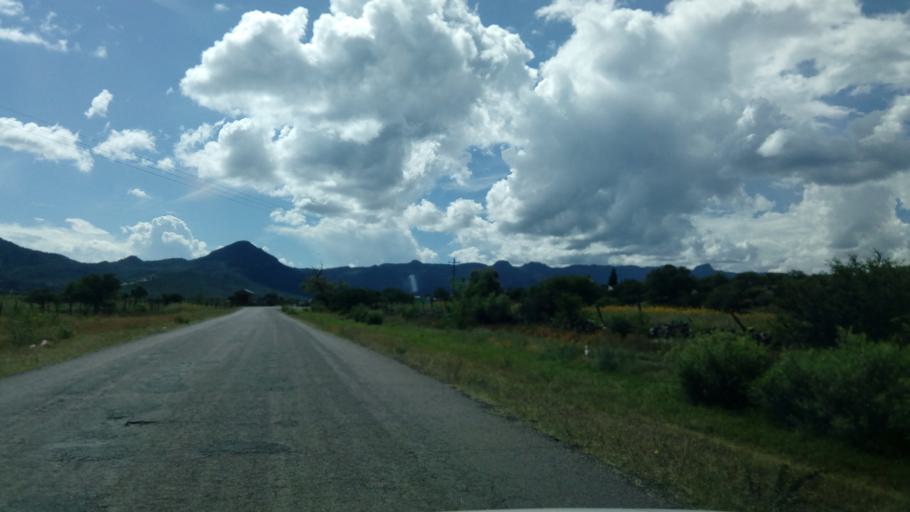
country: MX
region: Durango
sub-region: Durango
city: Jose Refugio Salcido
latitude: 23.7974
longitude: -104.4861
